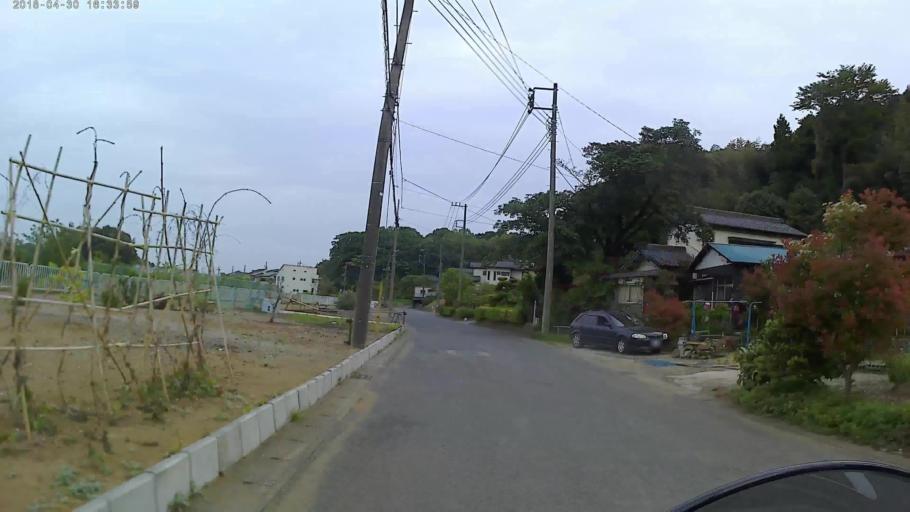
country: JP
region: Kanagawa
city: Zama
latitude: 35.4484
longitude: 139.4066
